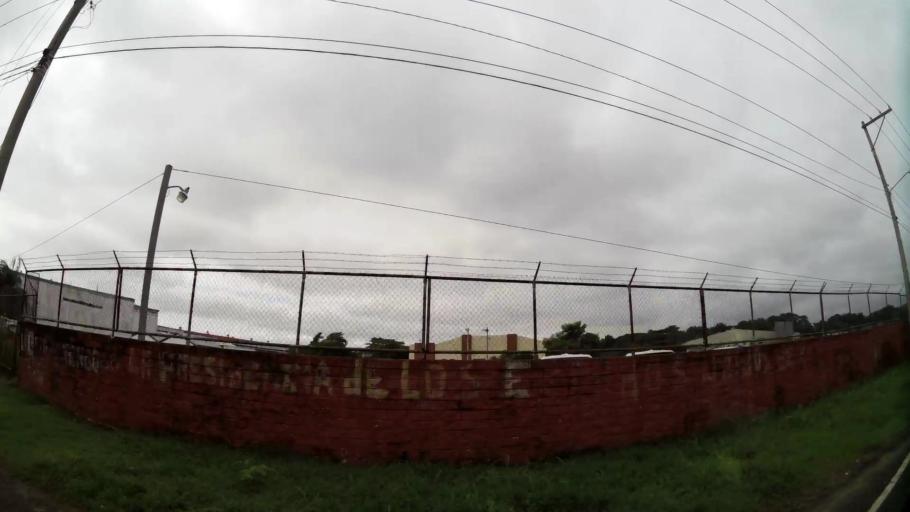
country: PA
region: Panama
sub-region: Distrito de Panama
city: Ancon
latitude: 8.9743
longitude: -79.5383
